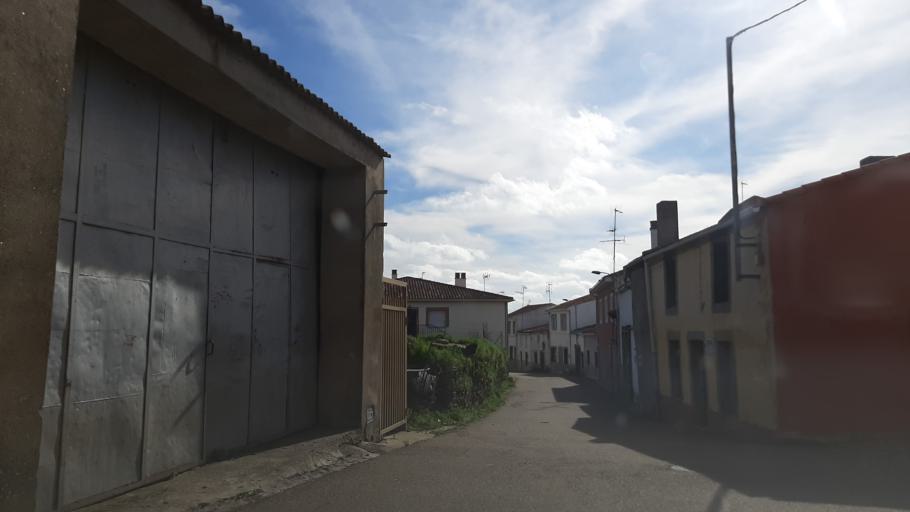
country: ES
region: Castille and Leon
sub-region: Provincia de Salamanca
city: Villarino de los Aires
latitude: 41.2377
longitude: -6.5227
